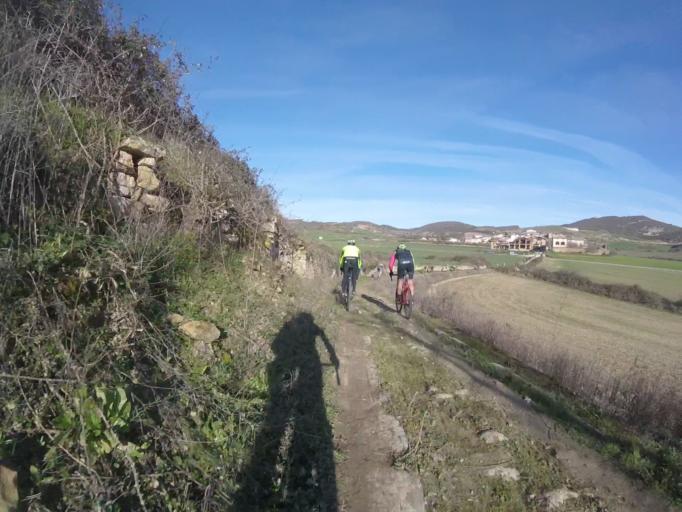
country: ES
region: Navarre
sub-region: Provincia de Navarra
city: Yerri
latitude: 42.6893
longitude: -1.9575
